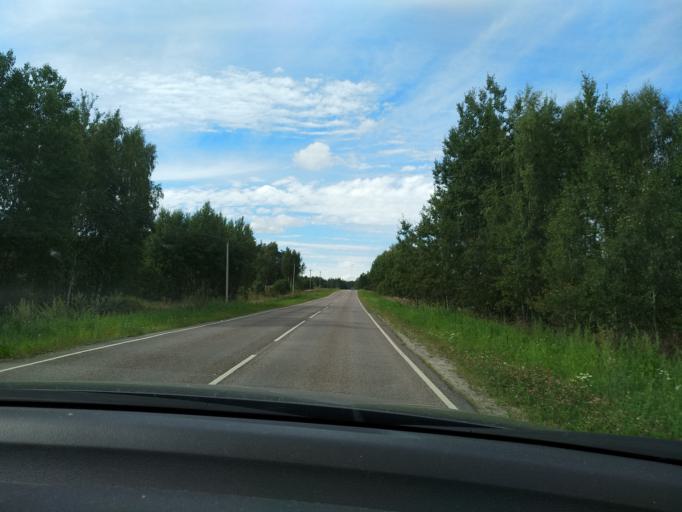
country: RU
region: Moskovskaya
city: Krasnyy Tkach
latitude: 55.3933
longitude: 39.1405
